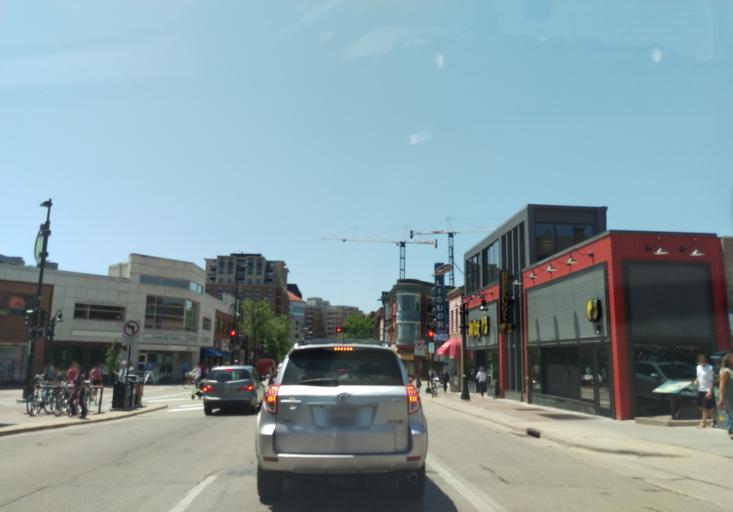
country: US
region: Wisconsin
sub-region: Dane County
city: Madison
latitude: 43.0751
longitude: -89.3913
